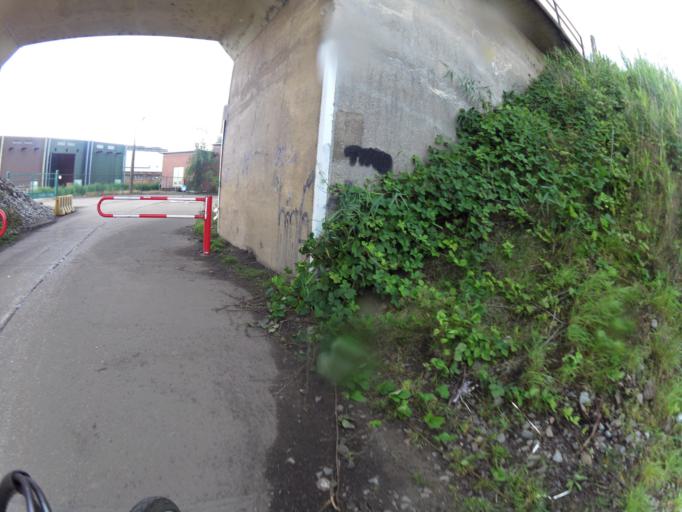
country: BE
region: Flanders
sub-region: Provincie Antwerpen
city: Balen
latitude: 51.2034
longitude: 5.2300
